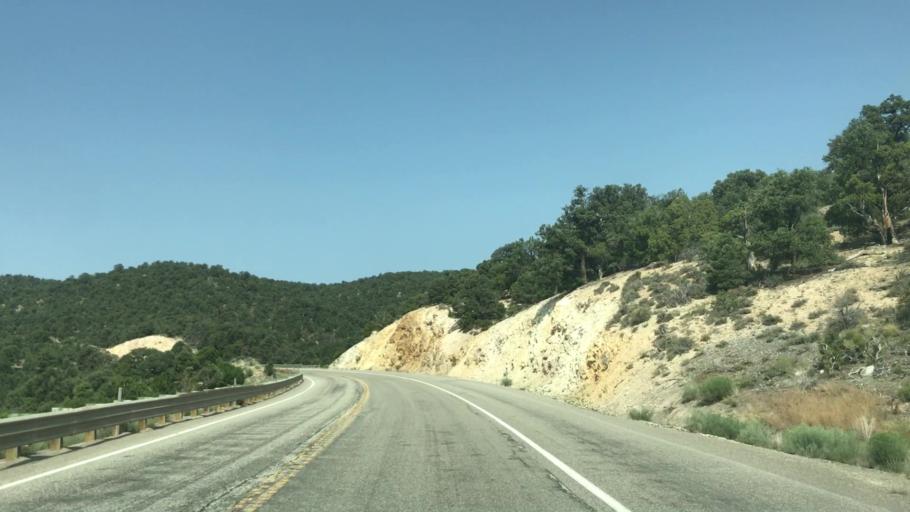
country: US
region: Nevada
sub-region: White Pine County
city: Ely
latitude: 39.0429
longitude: -114.6308
